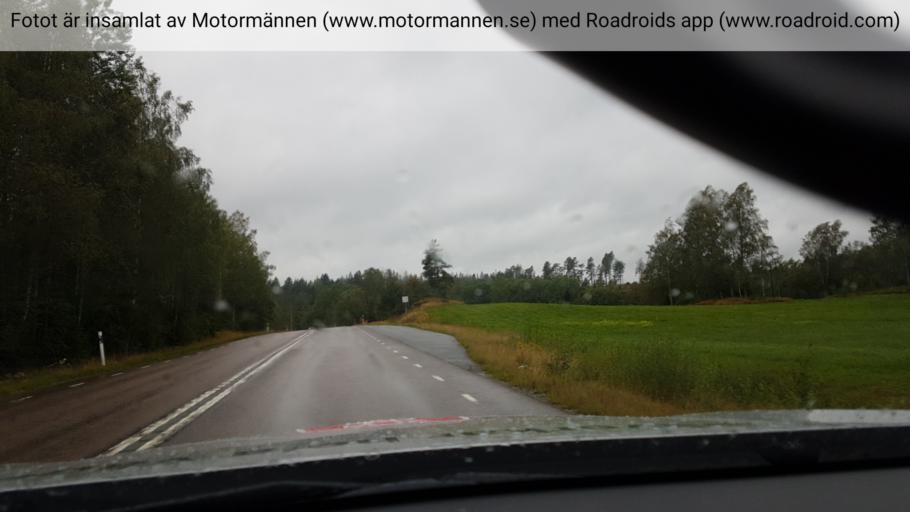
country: SE
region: Vaestra Goetaland
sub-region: Dals-Ed Kommun
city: Ed
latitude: 58.9215
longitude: 12.0281
